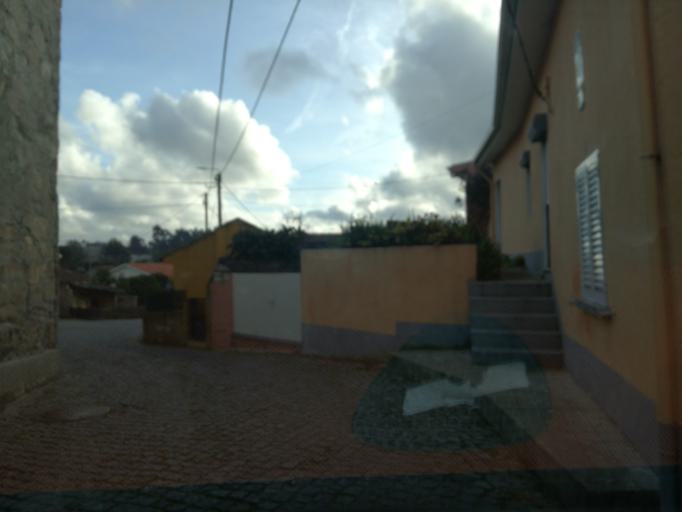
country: PT
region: Porto
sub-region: Maia
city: Nogueira
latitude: 41.2550
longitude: -8.6012
